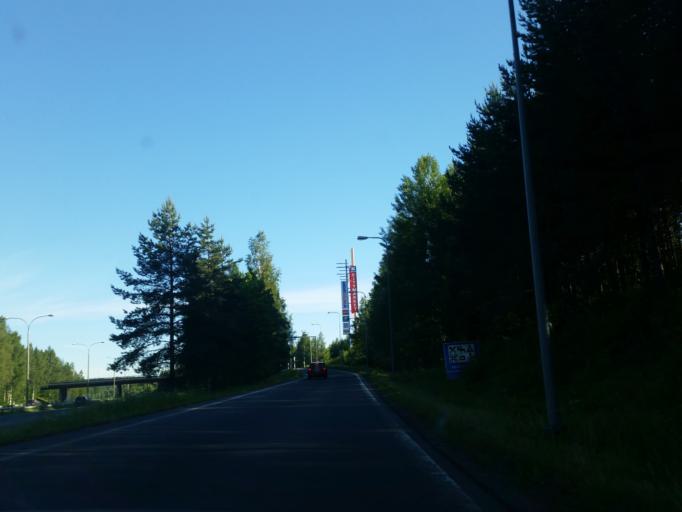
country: FI
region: Northern Savo
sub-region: Kuopio
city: Kuopio
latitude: 62.8642
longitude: 27.6177
